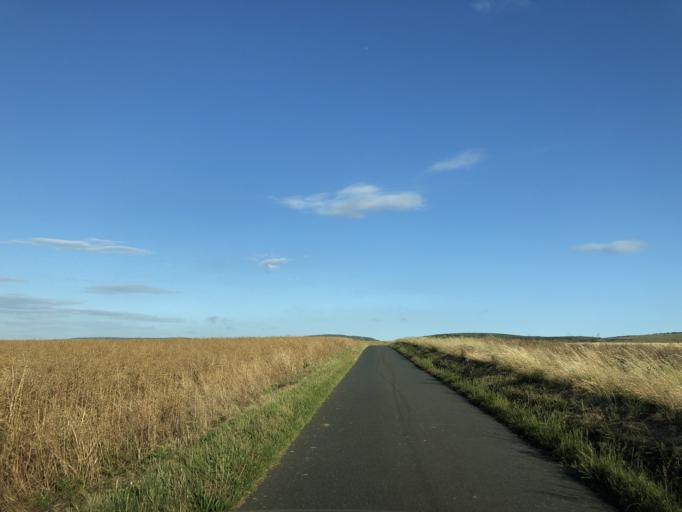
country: GB
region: England
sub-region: Isle of Wight
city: Yarmouth
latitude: 50.6833
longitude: -1.4672
